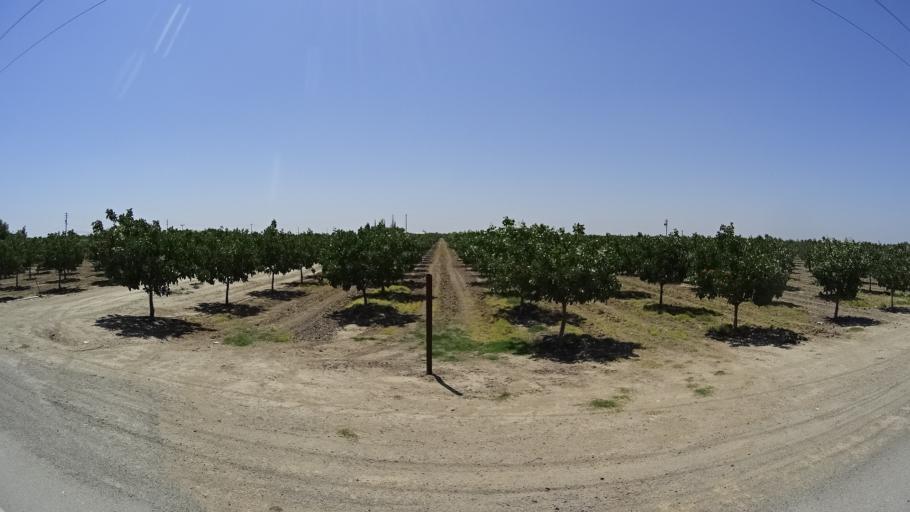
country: US
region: California
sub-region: Kings County
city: Lucerne
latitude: 36.4011
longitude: -119.6747
